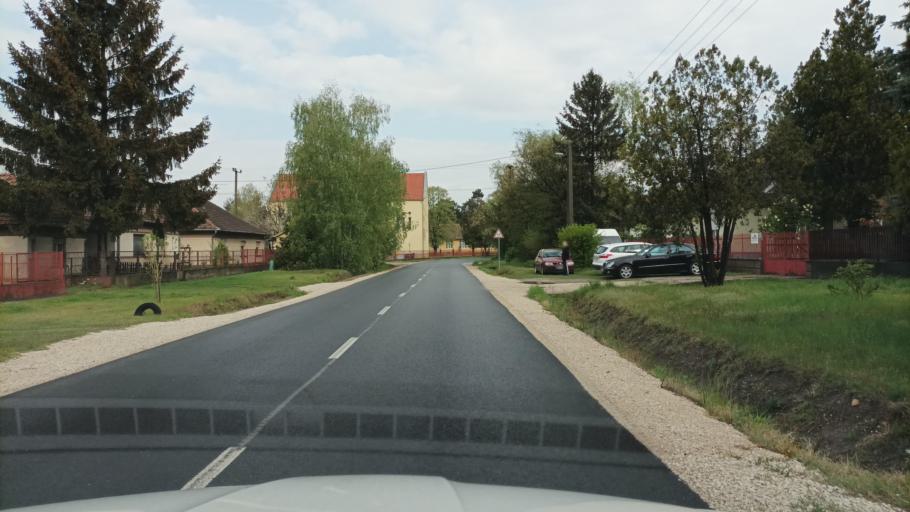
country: HU
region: Pest
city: Danszentmiklos
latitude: 47.1722
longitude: 19.5005
